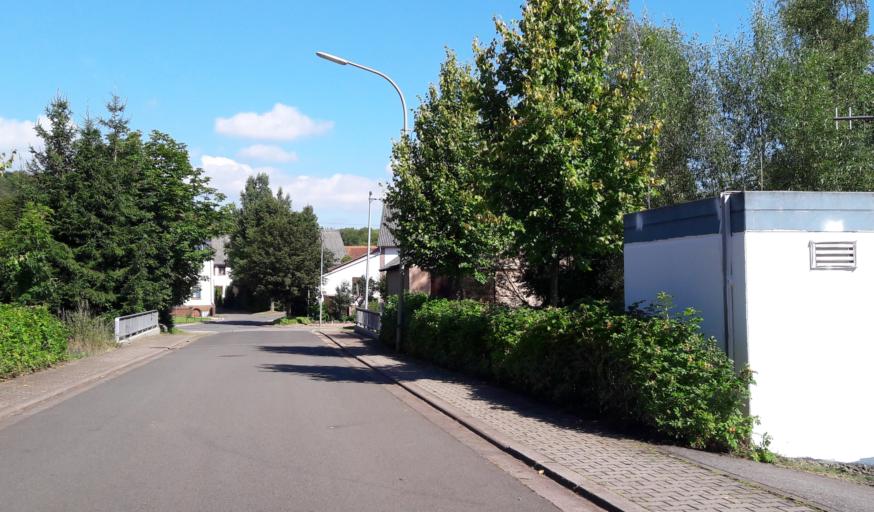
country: DE
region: Rheinland-Pfalz
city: Hahnweiler
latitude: 49.5523
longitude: 7.2025
